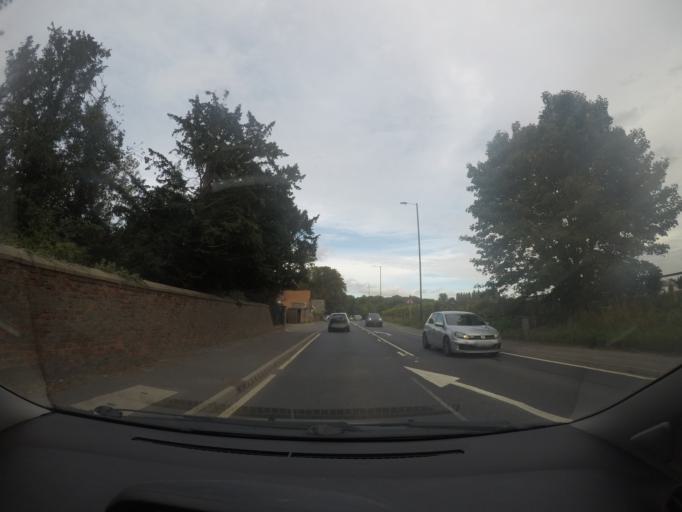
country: GB
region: England
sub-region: City of York
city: Deighton
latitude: 53.9099
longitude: -1.0501
